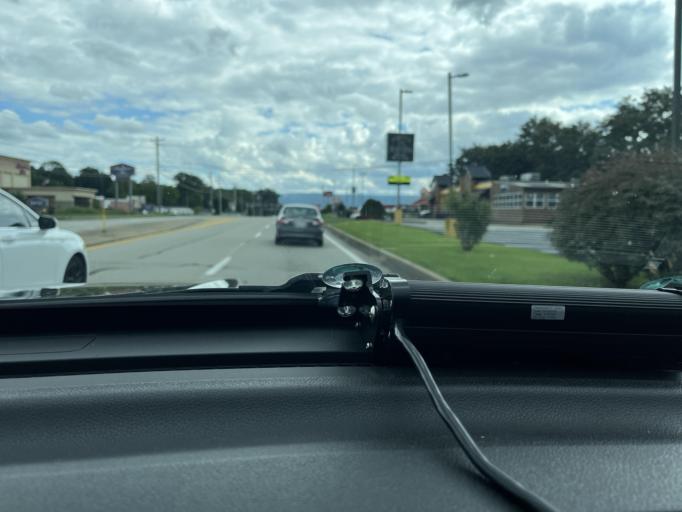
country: US
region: Pennsylvania
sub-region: Fayette County
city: South Uniontown
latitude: 39.9134
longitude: -79.7492
